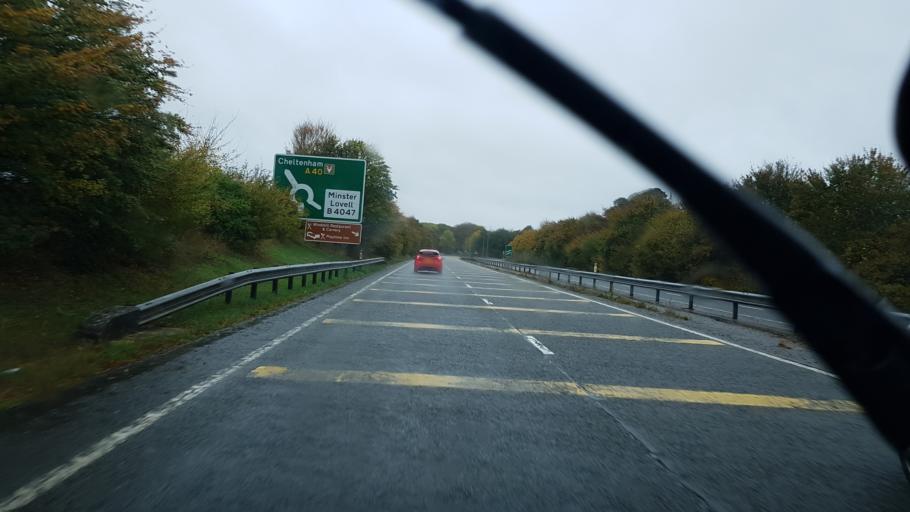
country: GB
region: England
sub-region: Oxfordshire
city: Carterton
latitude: 51.7879
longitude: -1.5789
